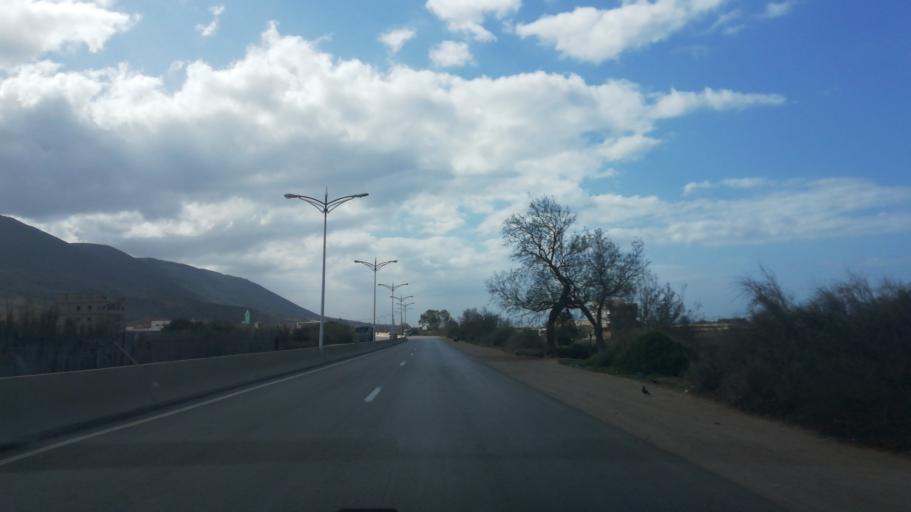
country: DZ
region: Mostaganem
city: Mostaganem
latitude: 36.0258
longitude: 0.1343
